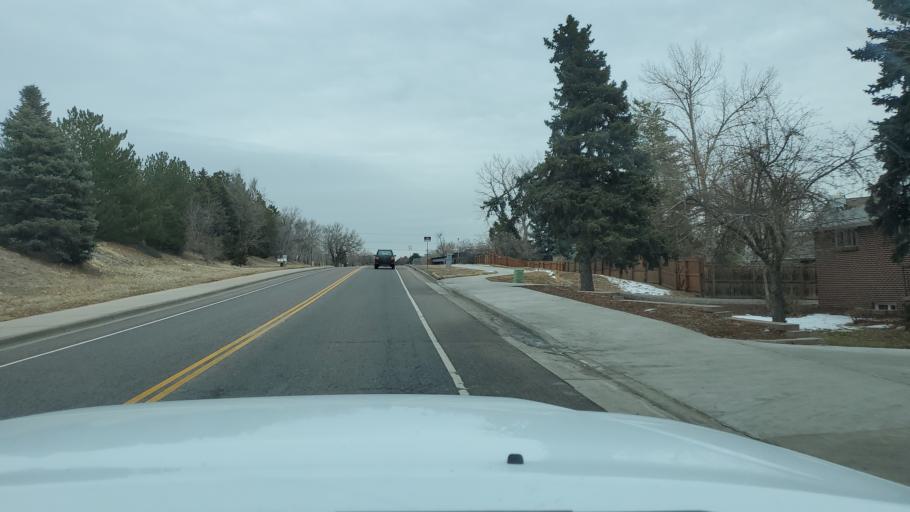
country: US
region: Colorado
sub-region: Arapahoe County
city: Castlewood
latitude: 39.6095
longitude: -104.9132
